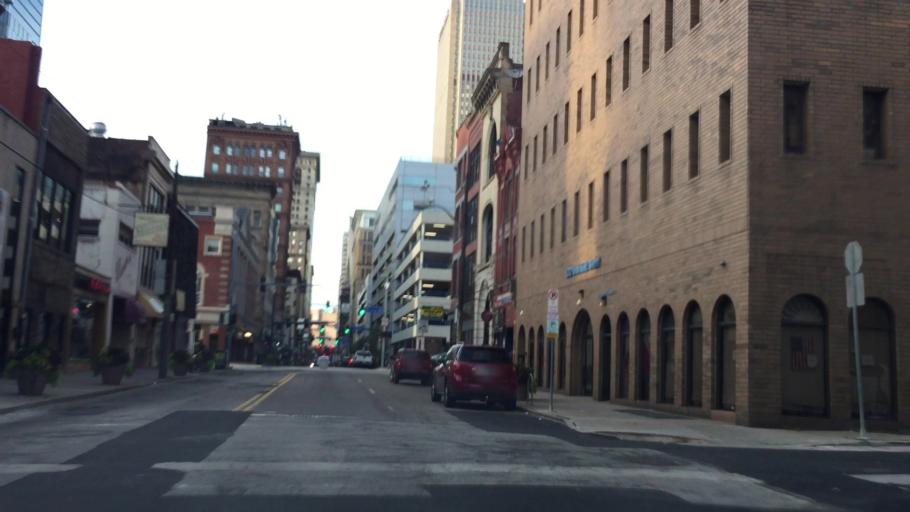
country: US
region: Pennsylvania
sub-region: Allegheny County
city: Pittsburgh
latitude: 40.4372
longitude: -80.0006
